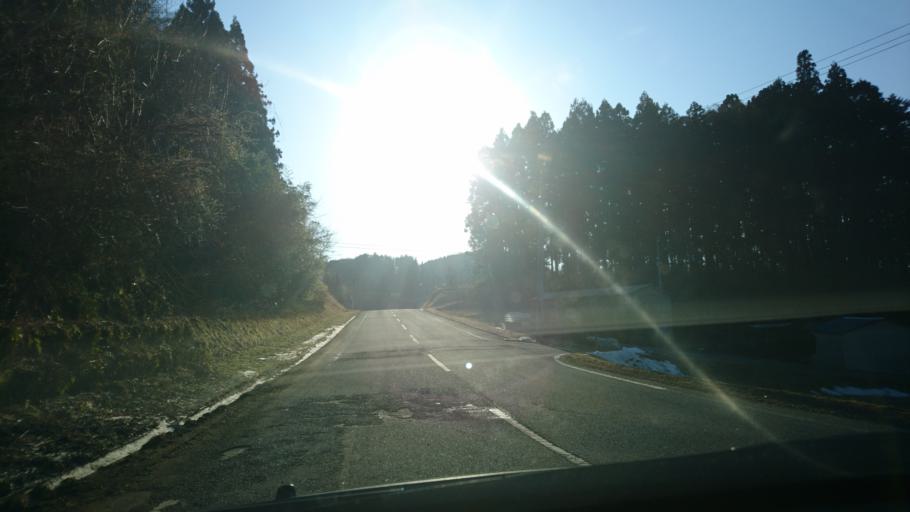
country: JP
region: Iwate
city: Ichinoseki
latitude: 38.8387
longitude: 141.3781
